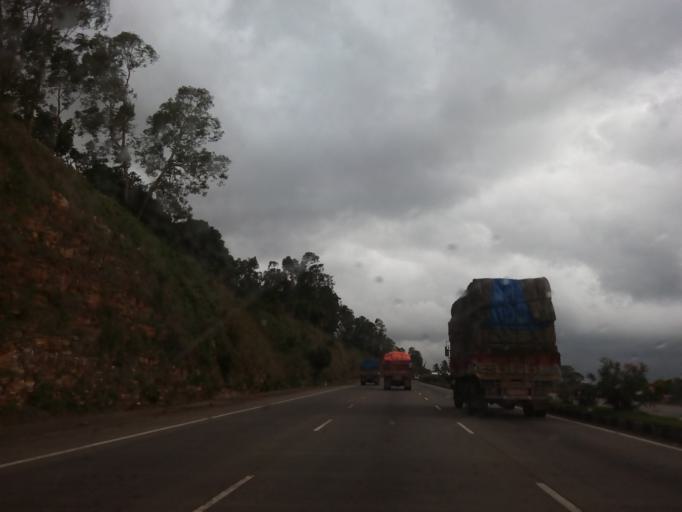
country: IN
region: Karnataka
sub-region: Belgaum
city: Belgaum
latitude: 16.0337
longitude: 74.5311
